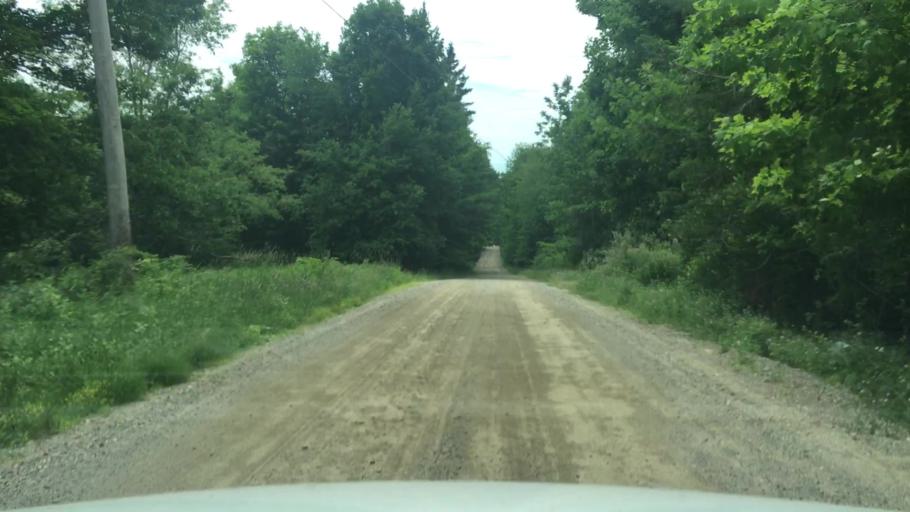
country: US
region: Maine
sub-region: Waldo County
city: Searsmont
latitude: 44.4323
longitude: -69.2542
